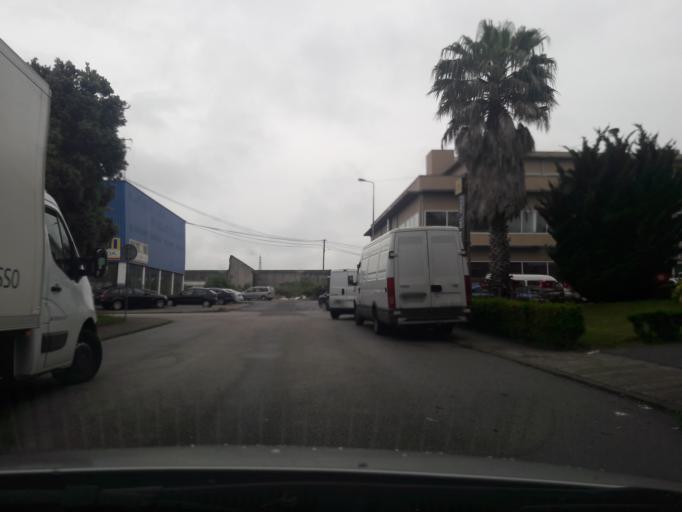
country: PT
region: Porto
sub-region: Vila do Conde
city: Arvore
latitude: 41.3273
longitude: -8.7161
